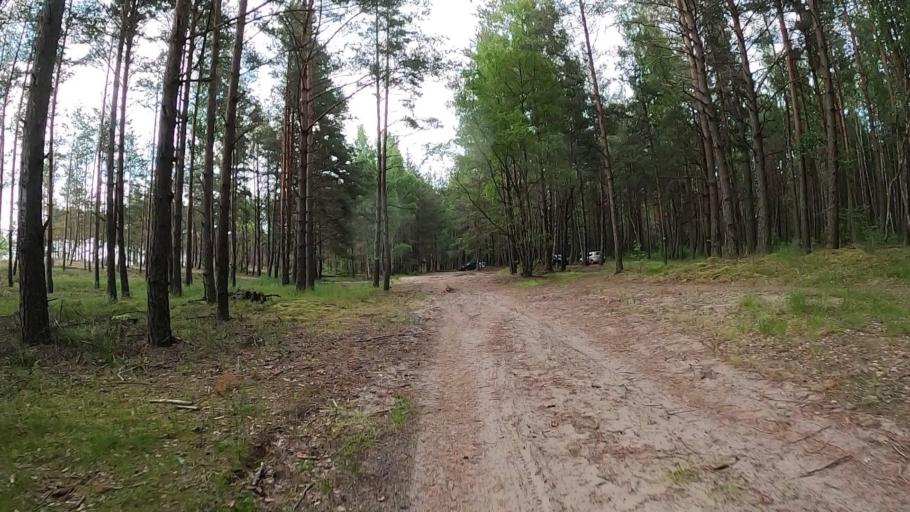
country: LV
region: Carnikava
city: Carnikava
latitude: 57.1496
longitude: 24.2516
